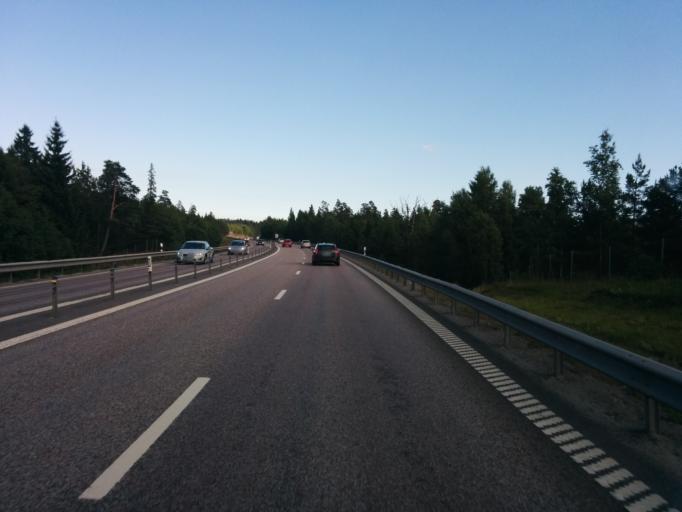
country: SE
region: Stockholm
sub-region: Varmdo Kommun
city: Gustavsberg
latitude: 59.3159
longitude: 18.3537
